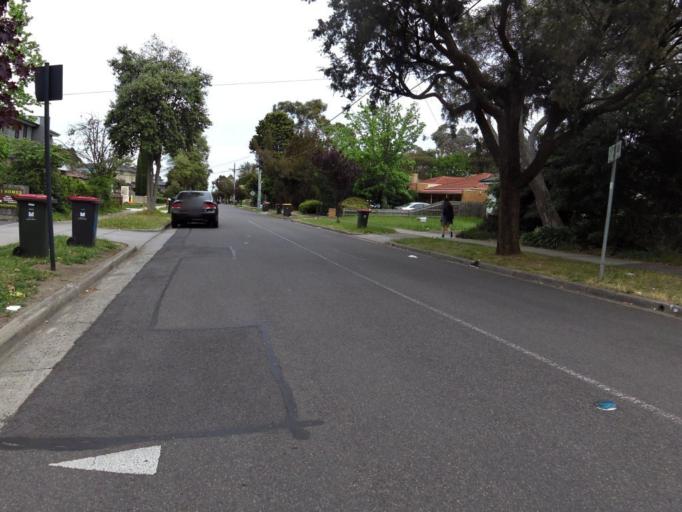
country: AU
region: Victoria
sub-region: Monash
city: Clayton
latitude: -37.9097
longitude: 145.1283
